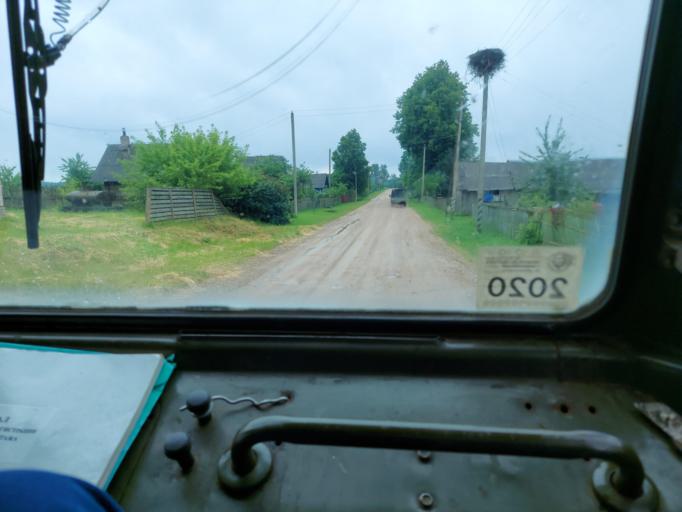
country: BY
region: Mogilev
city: Poselok Voskhod
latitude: 53.6839
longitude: 30.3875
